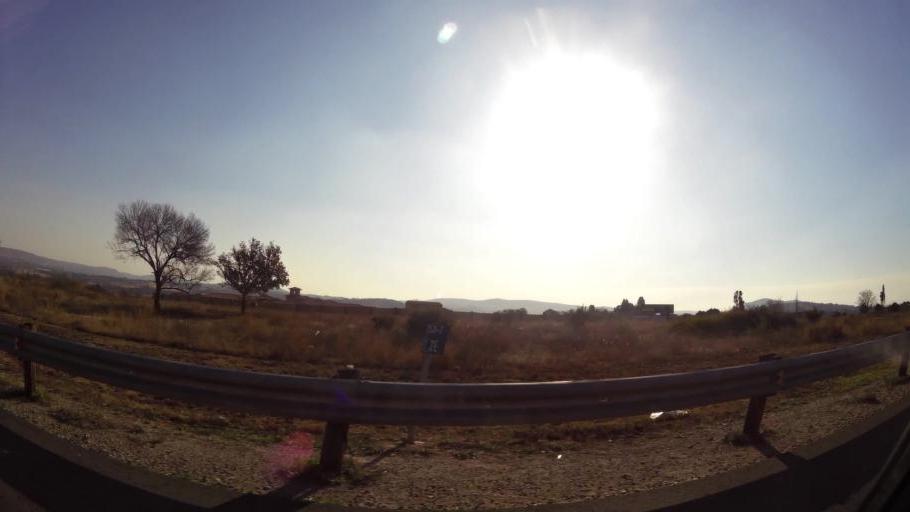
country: ZA
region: Gauteng
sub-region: West Rand District Municipality
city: Muldersdriseloop
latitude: -26.0283
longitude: 27.8495
